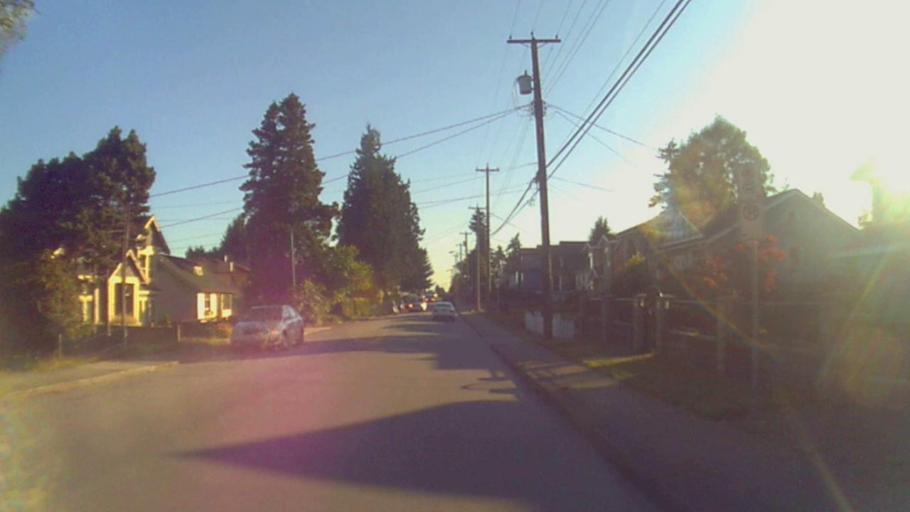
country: CA
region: British Columbia
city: New Westminster
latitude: 49.2237
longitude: -122.9237
